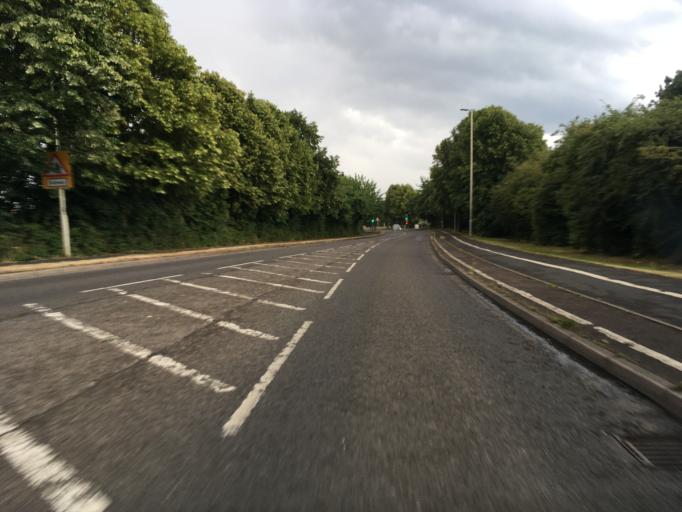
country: GB
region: England
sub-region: Gloucestershire
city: Barnwood
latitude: 51.8554
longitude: -2.2112
